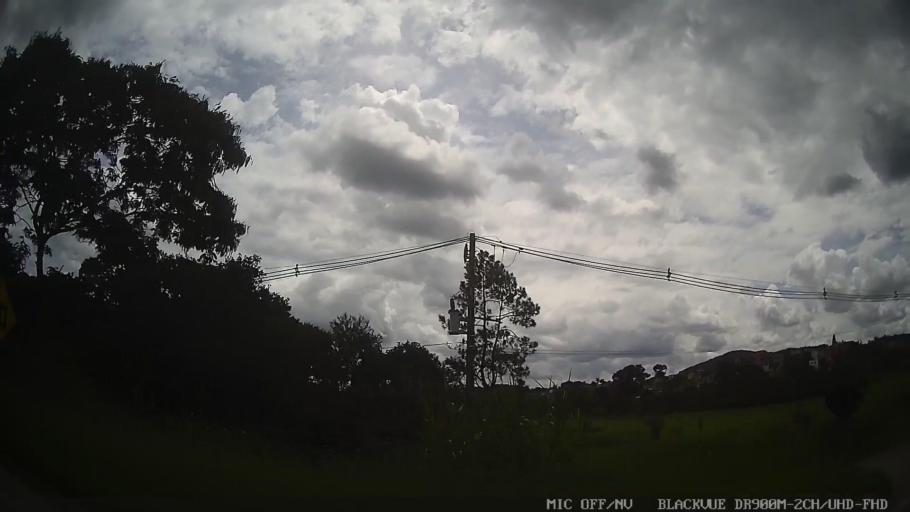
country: BR
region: Sao Paulo
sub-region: Suzano
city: Suzano
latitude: -23.6379
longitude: -46.3226
